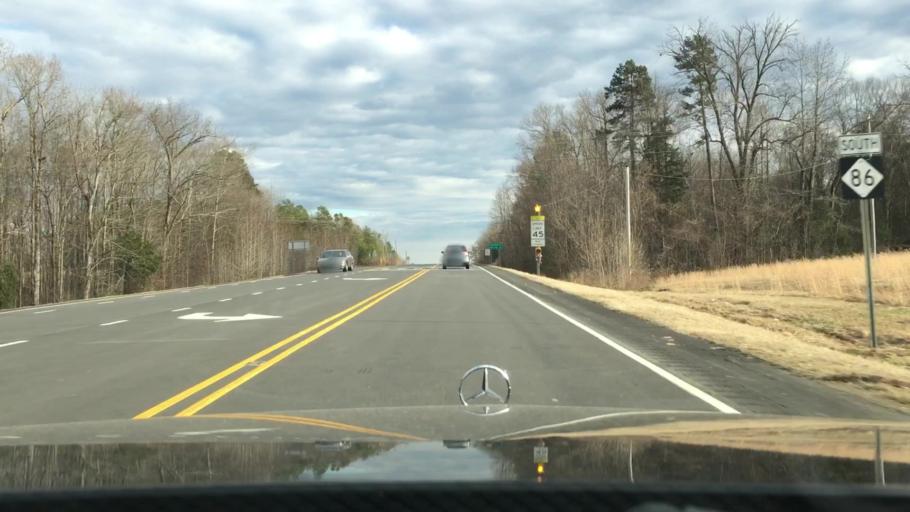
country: US
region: North Carolina
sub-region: Caswell County
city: Yanceyville
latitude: 36.3284
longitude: -79.2426
